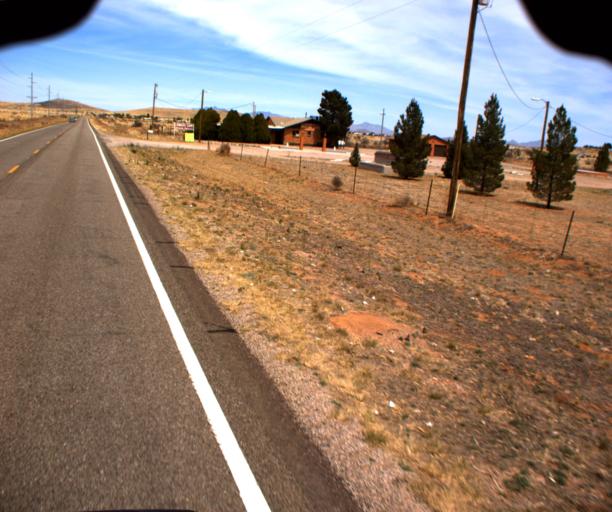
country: US
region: Arizona
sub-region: Cochise County
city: Willcox
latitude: 31.8718
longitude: -109.6951
